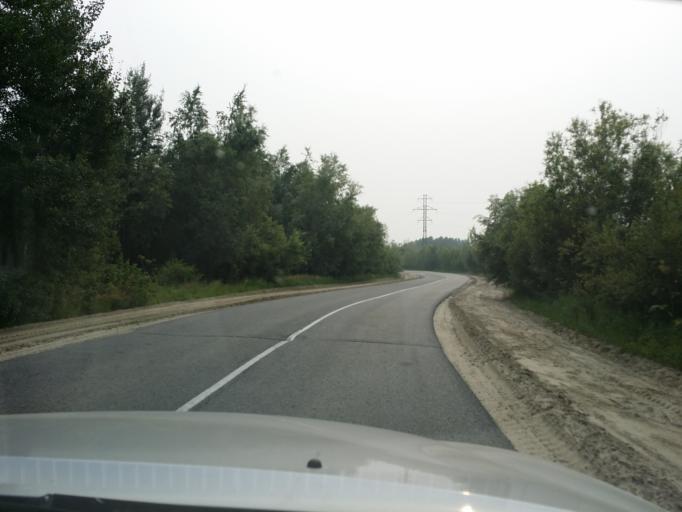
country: RU
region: Khanty-Mansiyskiy Avtonomnyy Okrug
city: Megion
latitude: 60.9983
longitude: 76.3030
